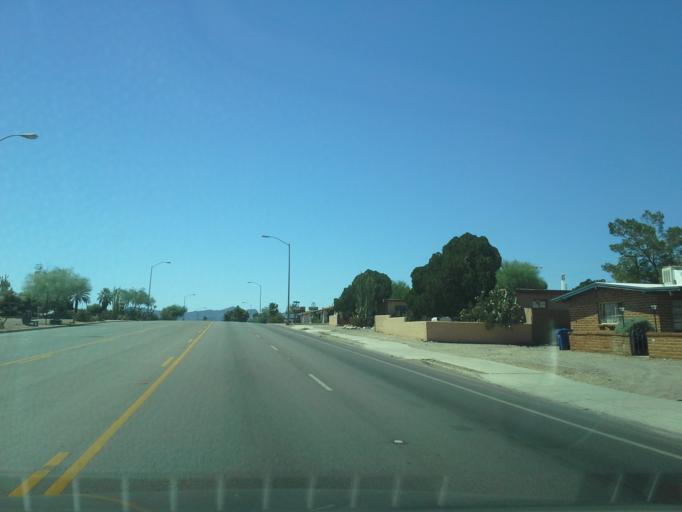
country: US
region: Arizona
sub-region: Pima County
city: Tucson
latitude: 32.2503
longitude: -110.9387
